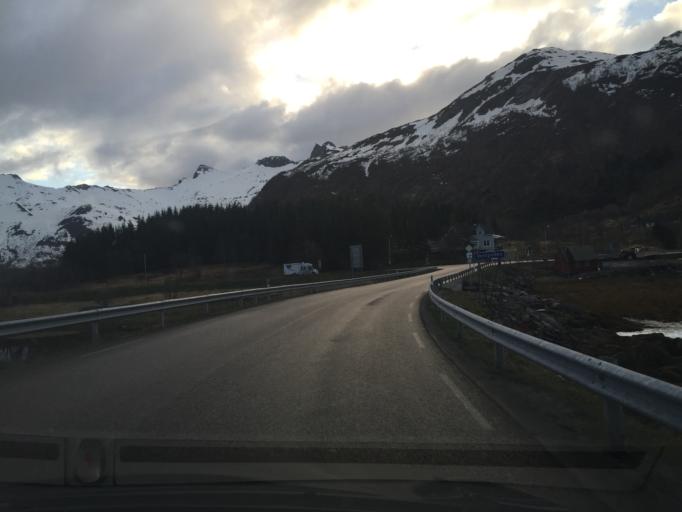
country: NO
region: Nordland
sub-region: Vagan
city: Svolvaer
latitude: 68.3244
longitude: 14.6890
